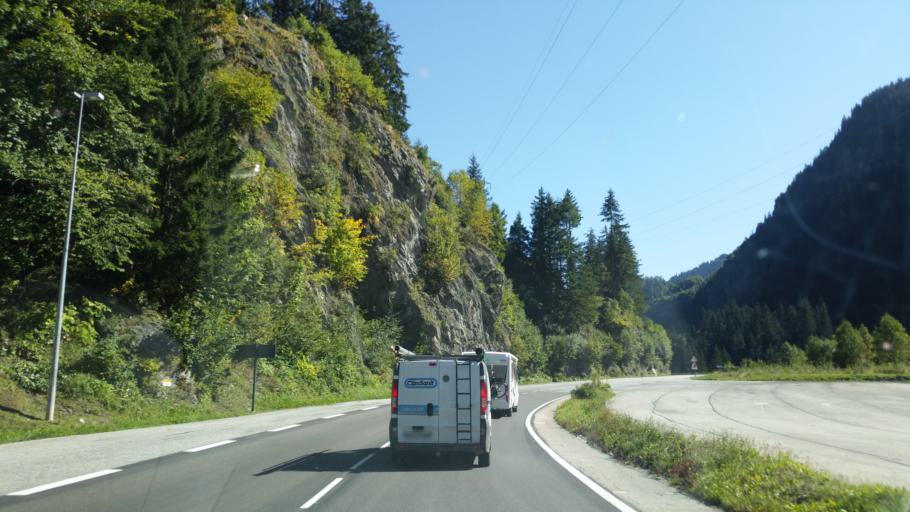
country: FR
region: Rhone-Alpes
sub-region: Departement de la Savoie
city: Tignes
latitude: 45.5615
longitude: 6.8942
